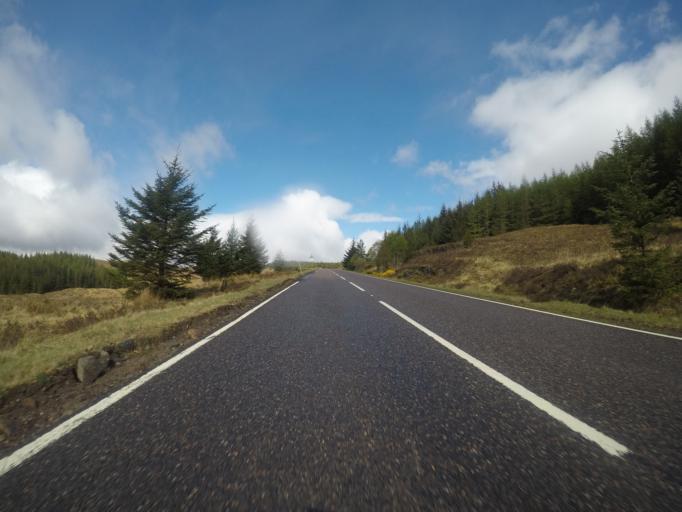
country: GB
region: Scotland
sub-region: Highland
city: Spean Bridge
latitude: 57.0910
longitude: -4.9839
